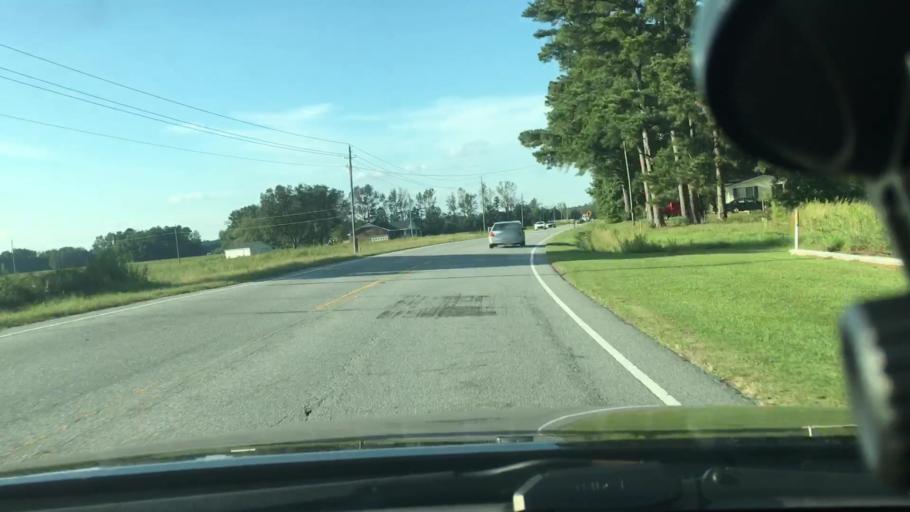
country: US
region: North Carolina
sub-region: Craven County
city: Vanceboro
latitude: 35.4237
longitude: -77.2605
